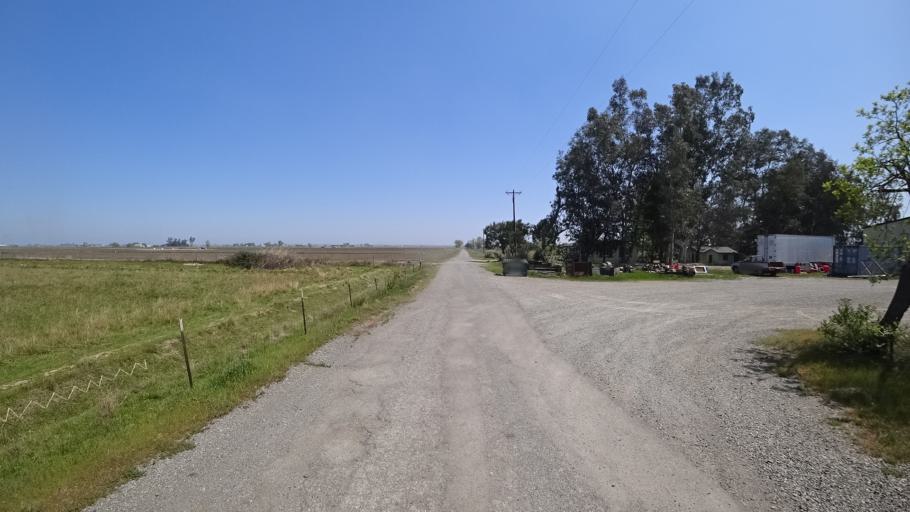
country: US
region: California
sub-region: Glenn County
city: Willows
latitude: 39.5508
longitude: -122.1009
